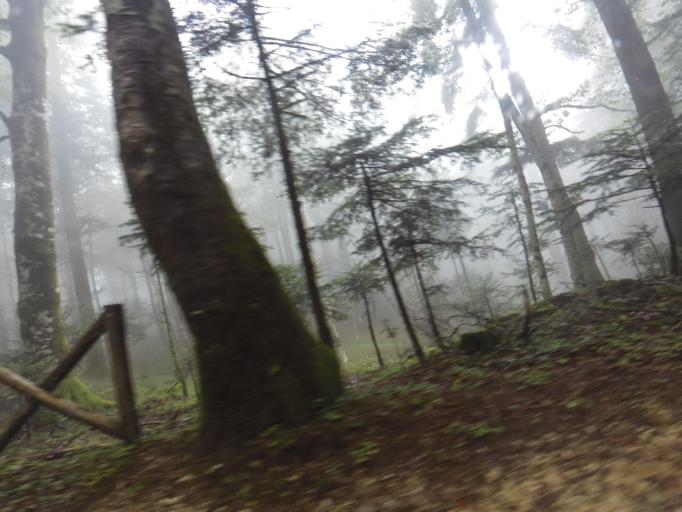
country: IT
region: Calabria
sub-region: Provincia di Vibo-Valentia
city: Mongiana
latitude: 38.5371
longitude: 16.3495
